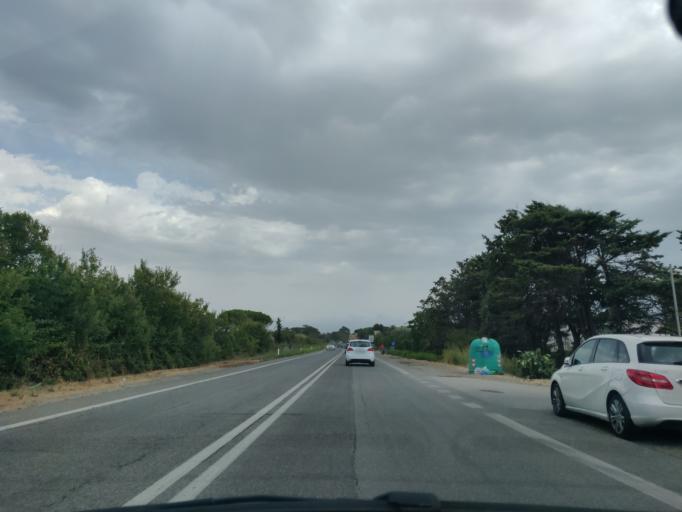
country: IT
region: Latium
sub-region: Citta metropolitana di Roma Capitale
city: Santa Marinella
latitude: 42.0340
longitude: 11.9299
